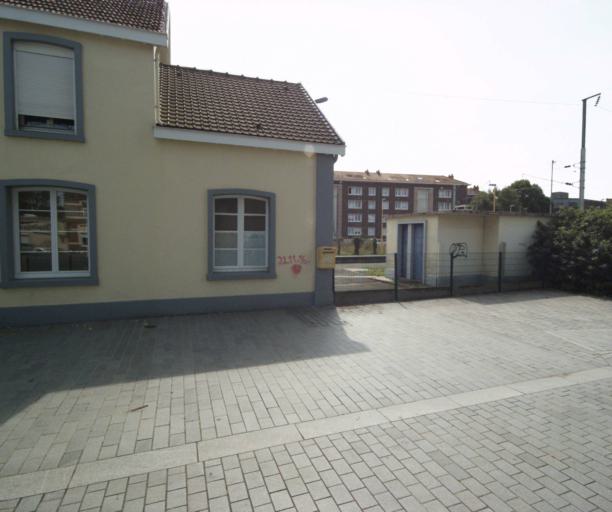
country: FR
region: Nord-Pas-de-Calais
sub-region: Departement du Nord
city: Loos
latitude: 50.6130
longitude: 3.0169
